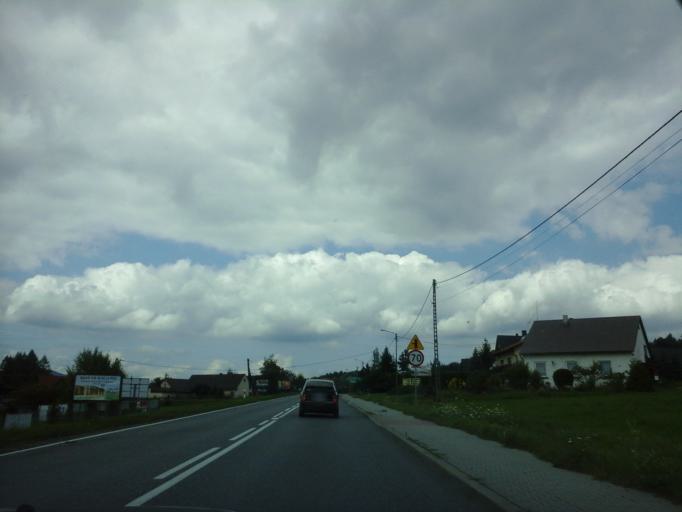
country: PL
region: Lesser Poland Voivodeship
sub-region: Powiat suski
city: Jordanow
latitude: 49.6577
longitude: 19.8095
